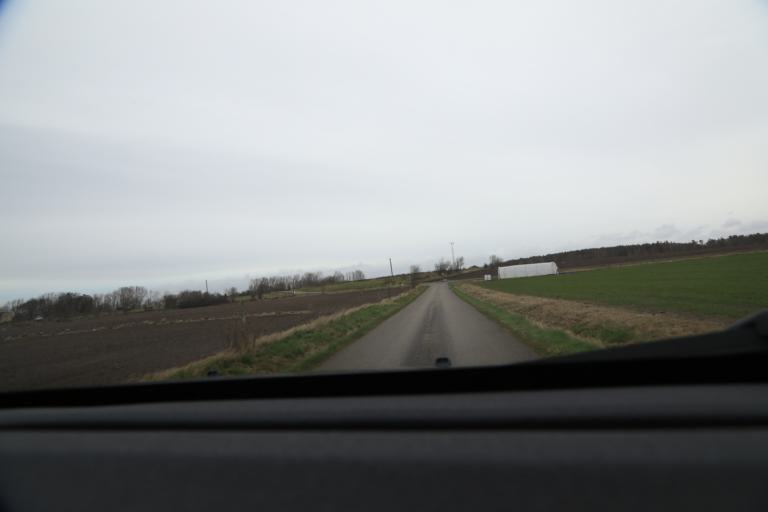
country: SE
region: Halland
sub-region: Varbergs Kommun
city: Traslovslage
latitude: 57.0759
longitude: 12.3028
